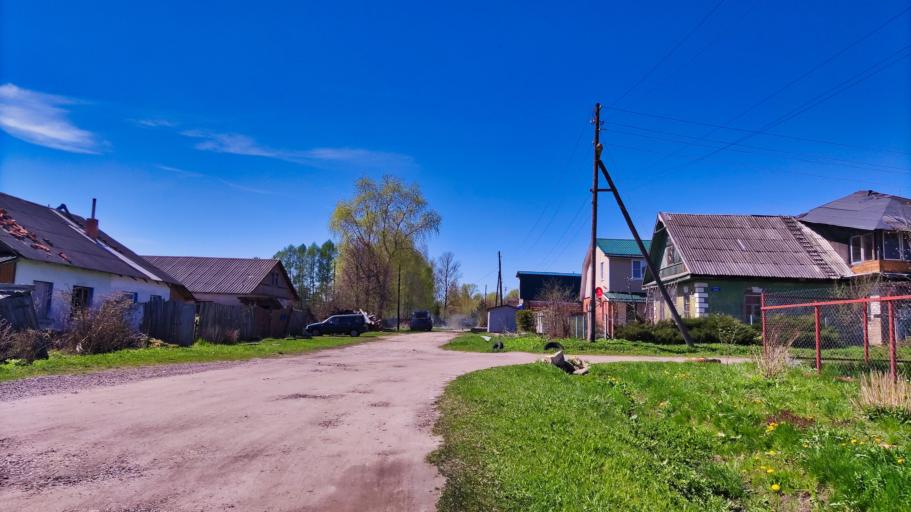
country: RU
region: Tverskaya
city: Rzhev
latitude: 56.2366
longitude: 34.3167
